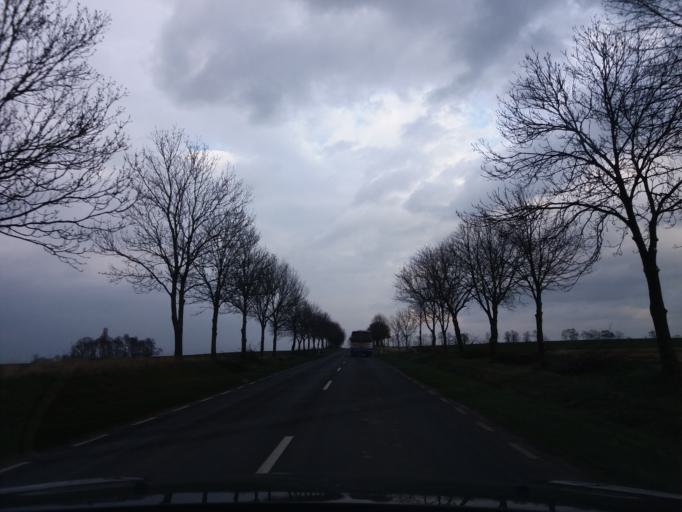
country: PL
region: West Pomeranian Voivodeship
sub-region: Powiat pyrzycki
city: Pyrzyce
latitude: 53.1367
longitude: 14.9385
